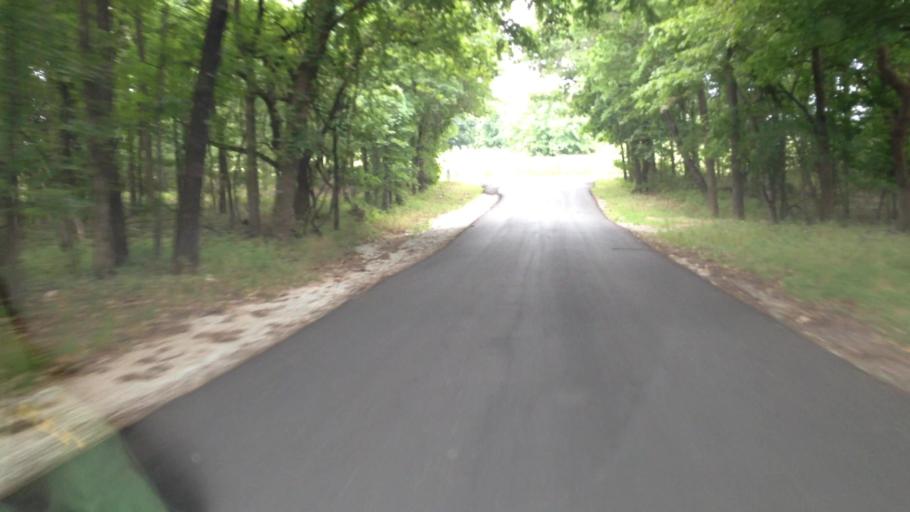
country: US
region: Oklahoma
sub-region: Delaware County
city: Cleora
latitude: 36.5473
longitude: -94.9641
